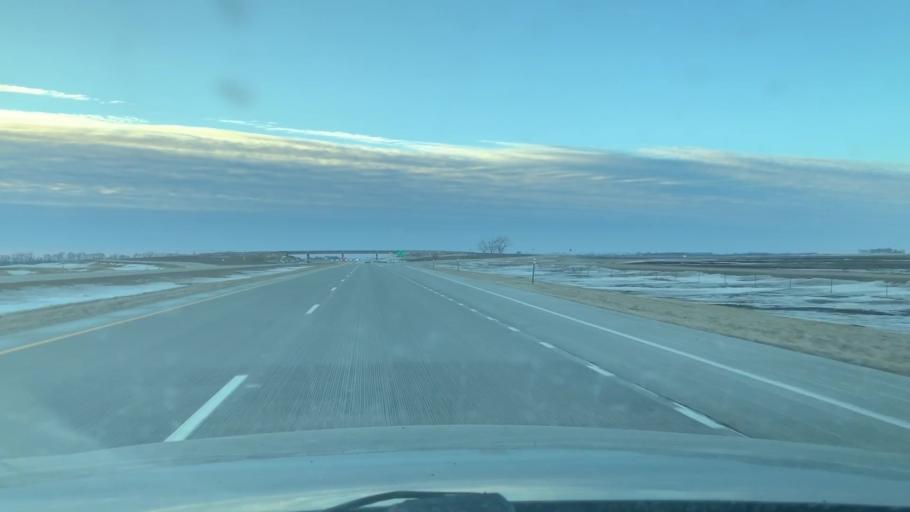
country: US
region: North Dakota
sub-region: Cass County
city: Casselton
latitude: 46.8758
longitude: -97.4868
